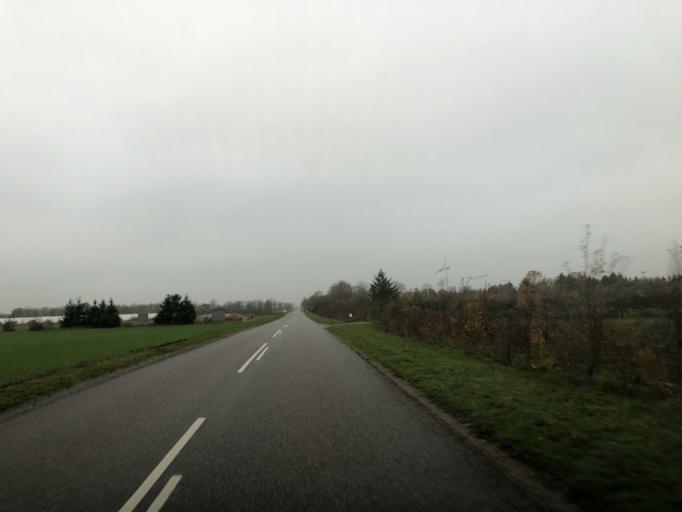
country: DK
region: Central Jutland
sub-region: Herning Kommune
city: Sunds
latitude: 56.2137
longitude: 8.9860
